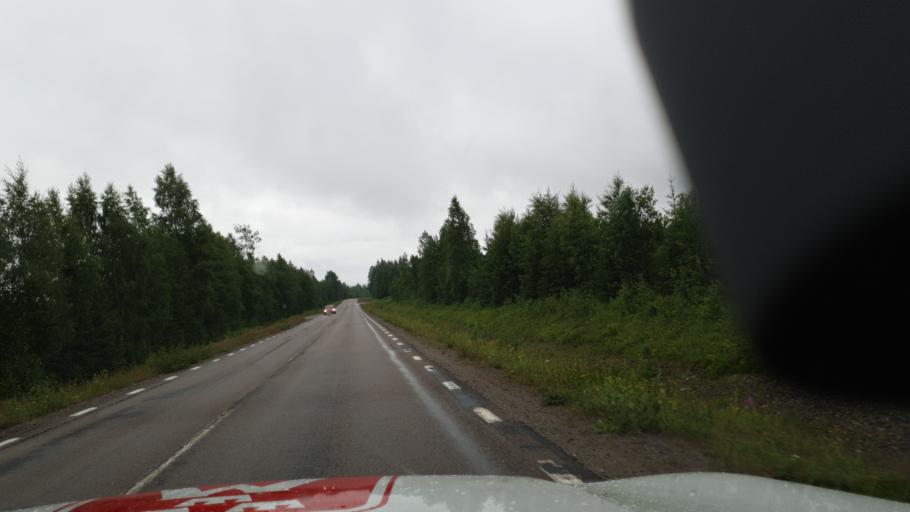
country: SE
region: Vaesterbotten
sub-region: Vannas Kommun
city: Vaennaes
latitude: 63.7947
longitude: 19.8083
